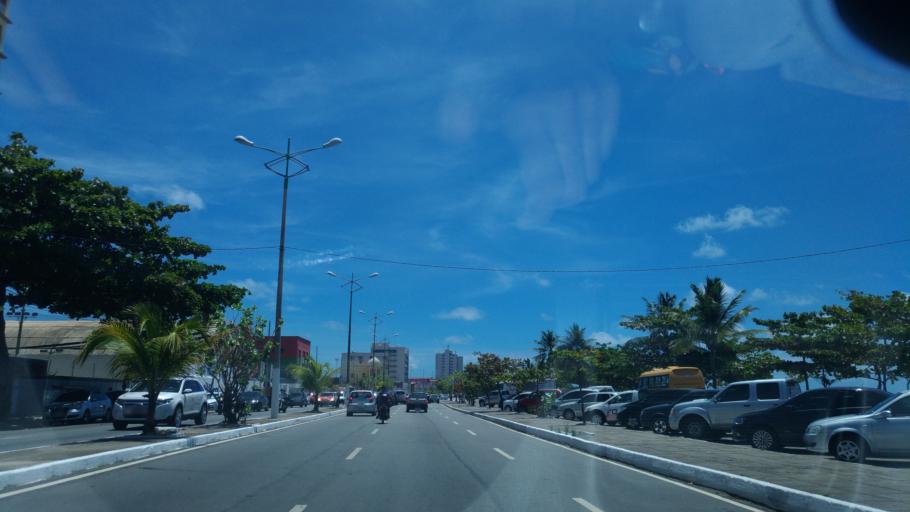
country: BR
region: Alagoas
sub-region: Maceio
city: Maceio
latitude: -9.6697
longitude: -35.7353
